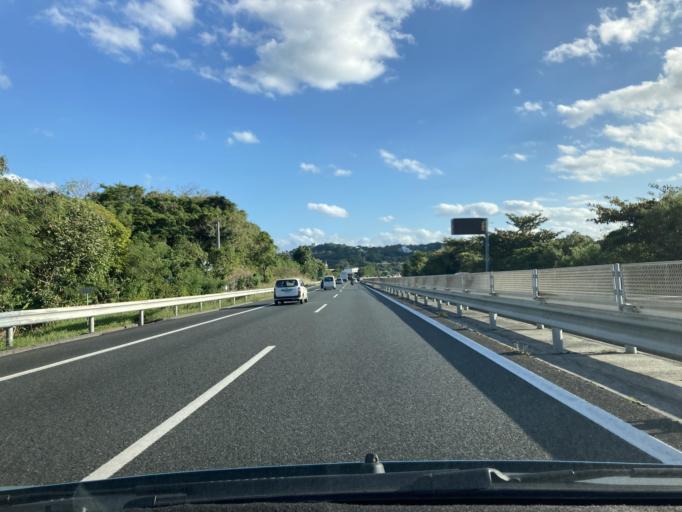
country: JP
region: Okinawa
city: Chatan
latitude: 26.3047
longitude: 127.7911
